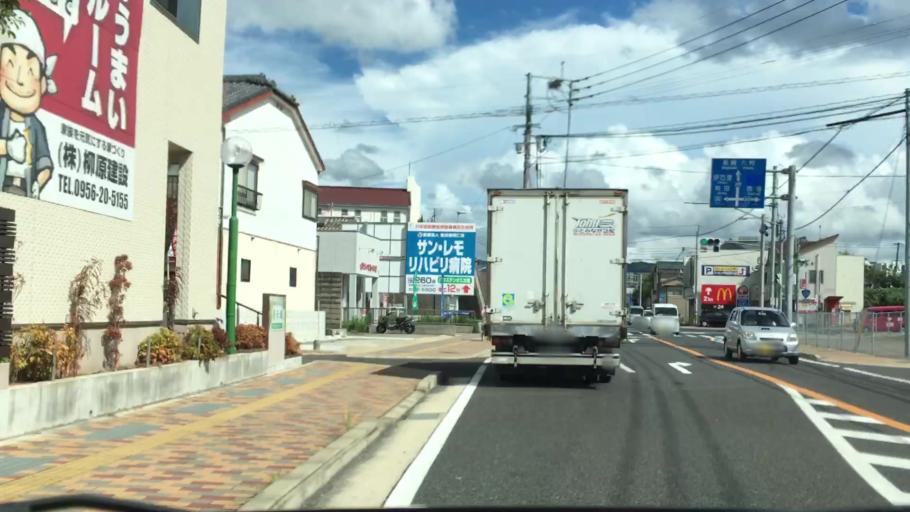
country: JP
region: Nagasaki
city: Sasebo
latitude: 33.1387
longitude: 129.7940
